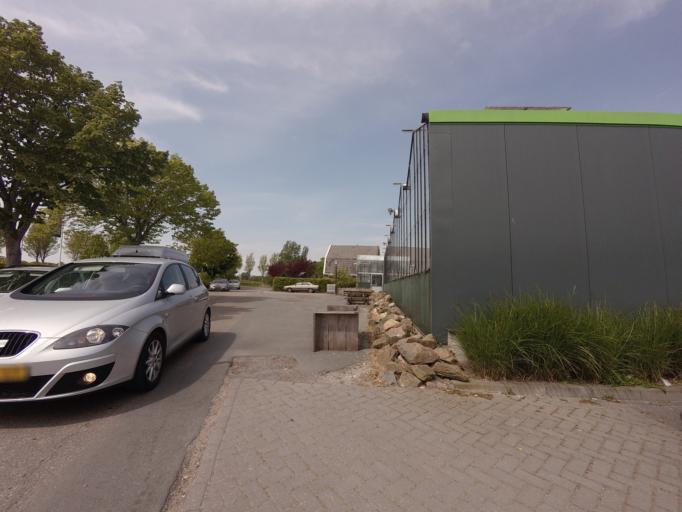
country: NL
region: Friesland
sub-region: Sudwest Fryslan
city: Bolsward
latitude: 53.1002
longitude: 5.4812
